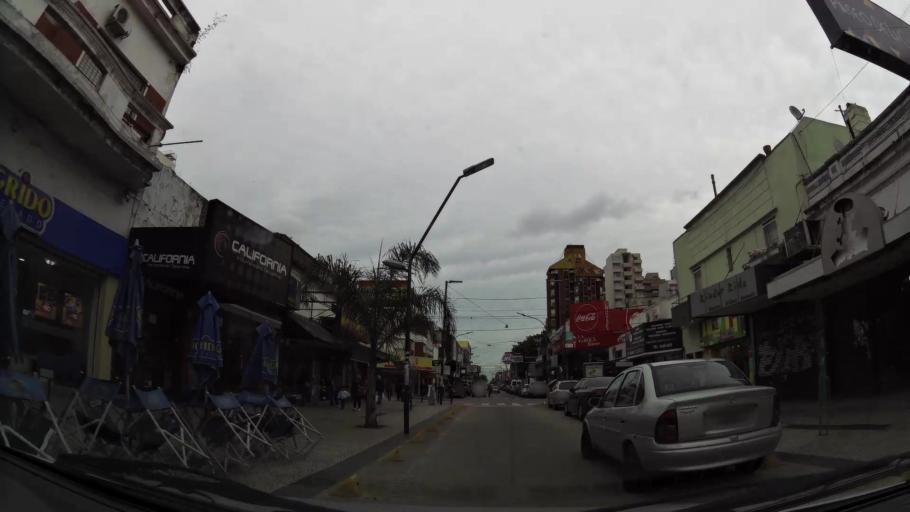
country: AR
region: Buenos Aires
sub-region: Partido de Lanus
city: Lanus
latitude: -34.7110
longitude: -58.3860
